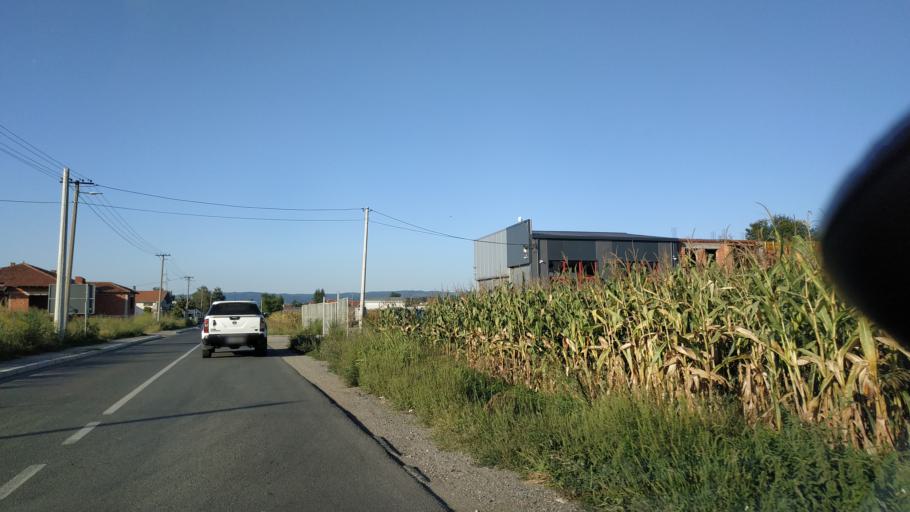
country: RS
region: Central Serbia
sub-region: Rasinski Okrug
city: Krusevac
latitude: 43.5328
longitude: 21.3426
